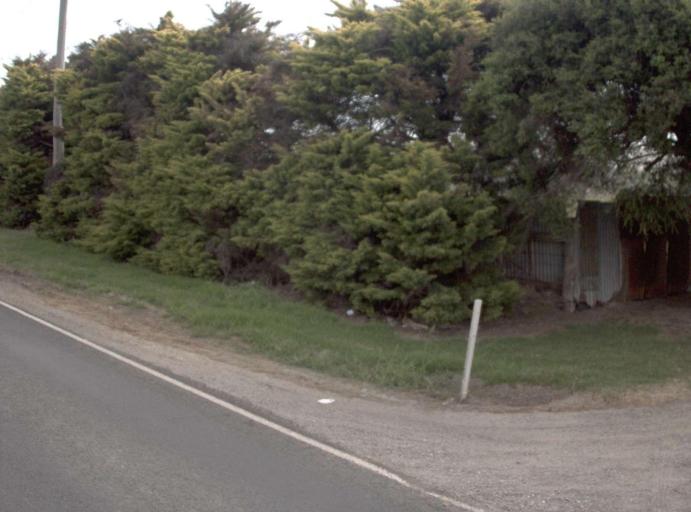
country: AU
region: Victoria
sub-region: Casey
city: Junction Village
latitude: -38.1283
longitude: 145.3253
